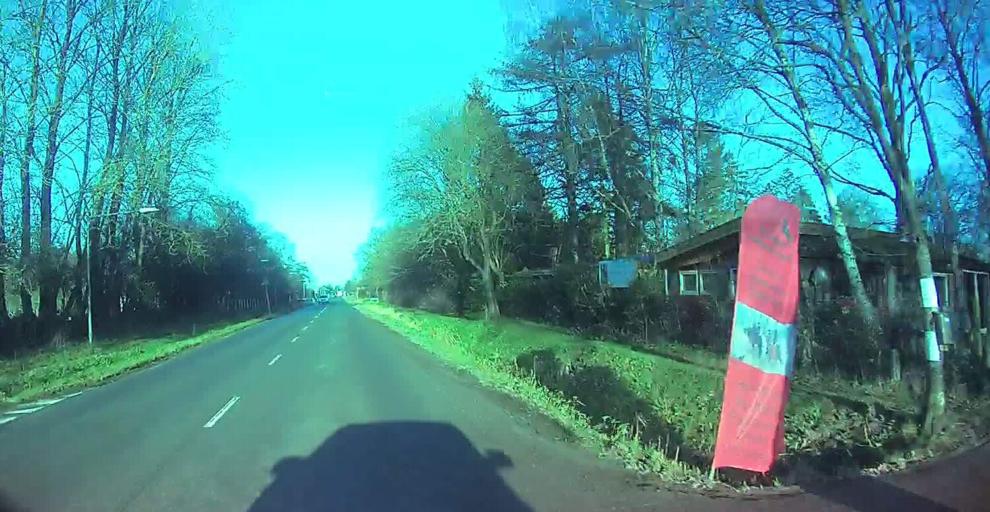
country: DK
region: Capital Region
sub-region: Tarnby Kommune
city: Tarnby
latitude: 55.5843
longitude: 12.5788
